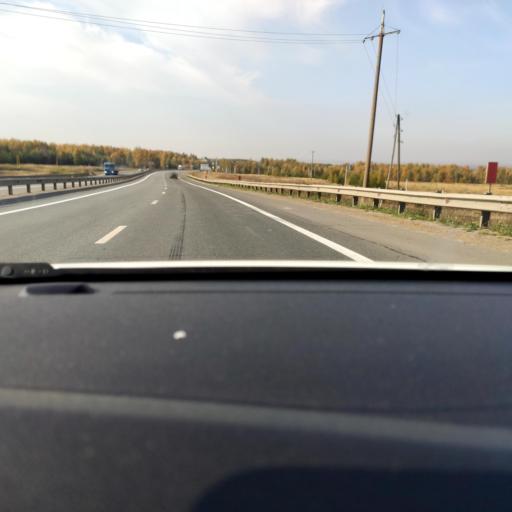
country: RU
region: Tatarstan
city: Vysokaya Gora
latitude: 55.8748
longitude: 49.2864
